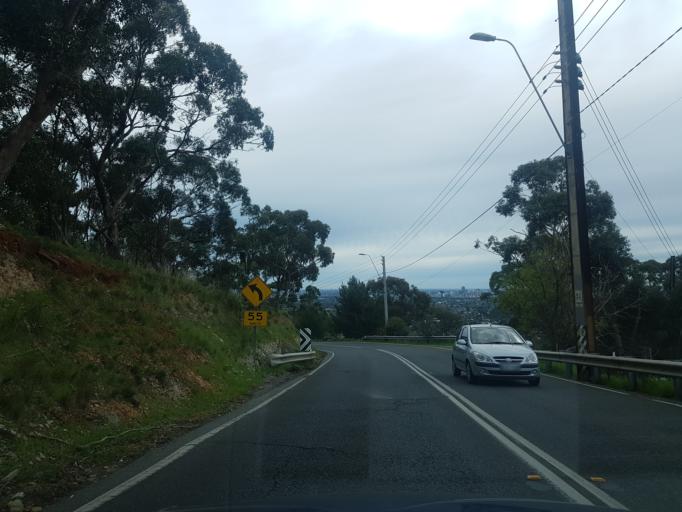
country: AU
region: South Australia
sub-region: Mitcham
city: Mitcham
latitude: -34.9871
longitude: 138.6247
